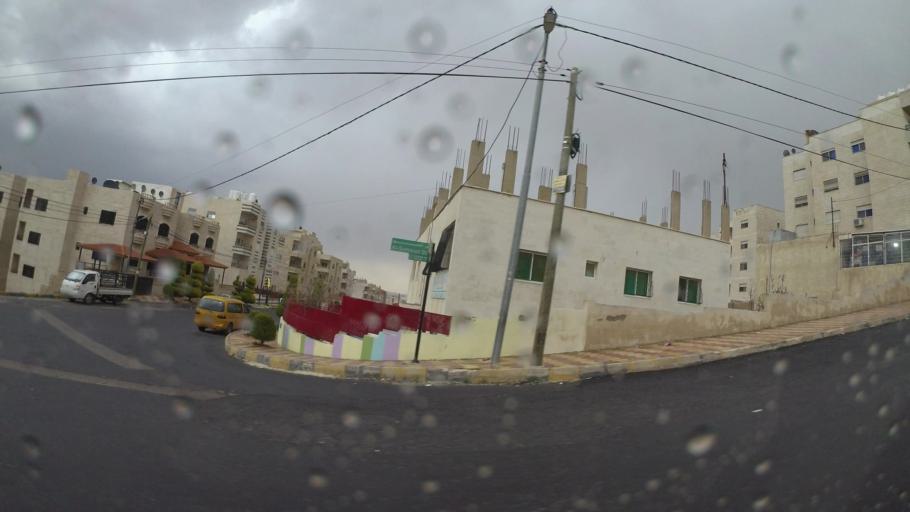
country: JO
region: Amman
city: Amman
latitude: 32.0100
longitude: 35.9572
